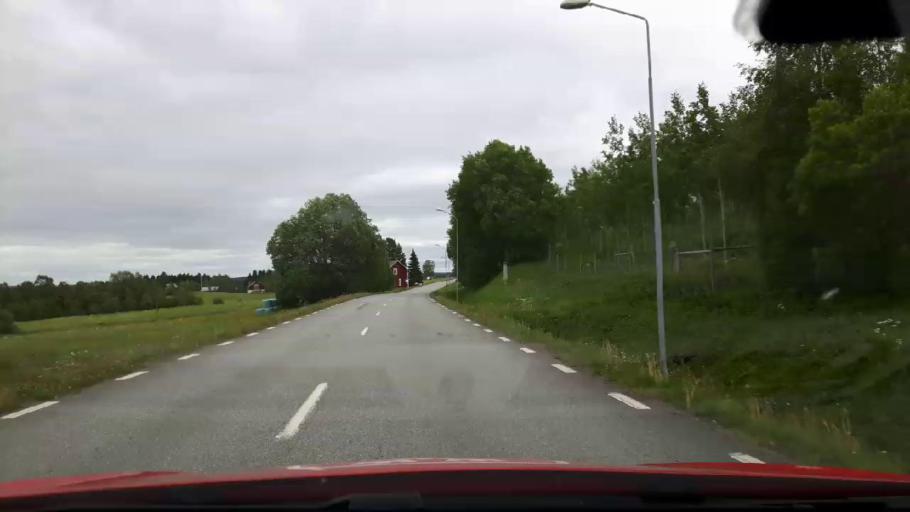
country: SE
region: Jaemtland
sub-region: Stroemsunds Kommun
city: Stroemsund
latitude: 63.5706
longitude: 15.3853
